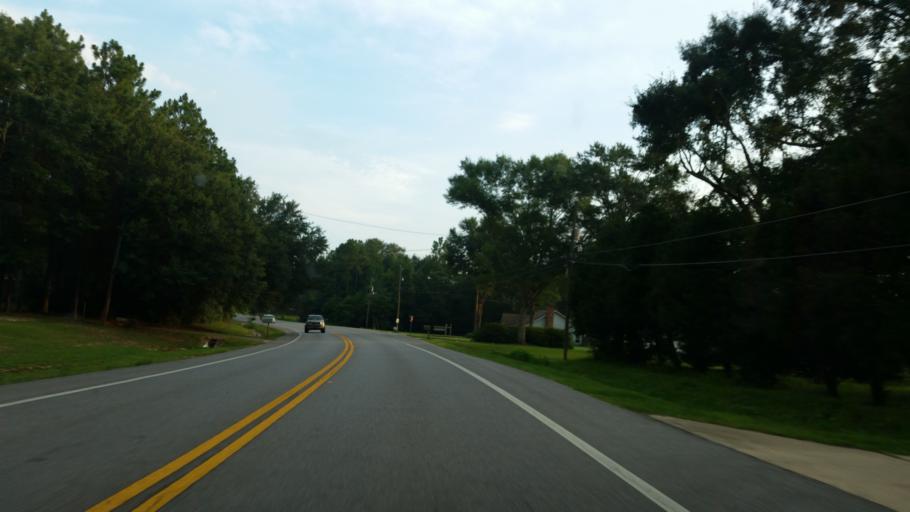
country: US
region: Florida
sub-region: Escambia County
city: Cantonment
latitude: 30.5948
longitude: -87.3491
